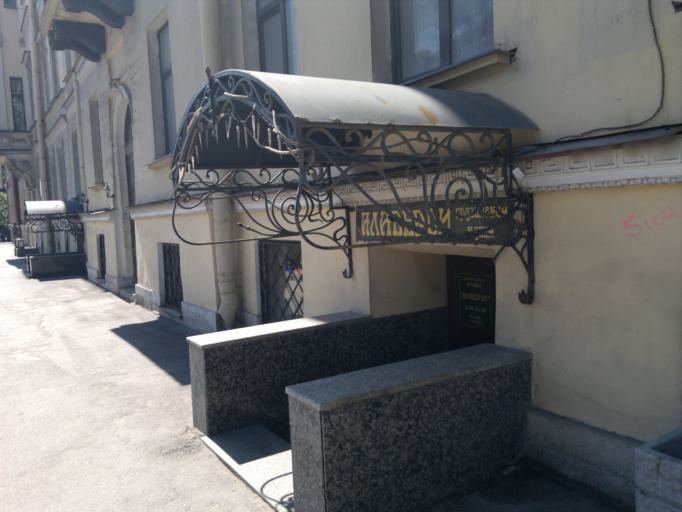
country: RU
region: St.-Petersburg
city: Saint Petersburg
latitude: 59.9399
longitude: 30.2923
